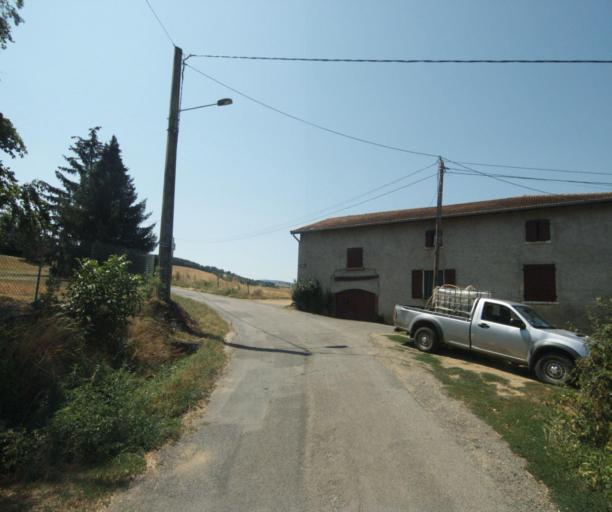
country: FR
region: Rhone-Alpes
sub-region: Departement du Rhone
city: Sain-Bel
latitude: 45.7967
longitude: 4.5969
